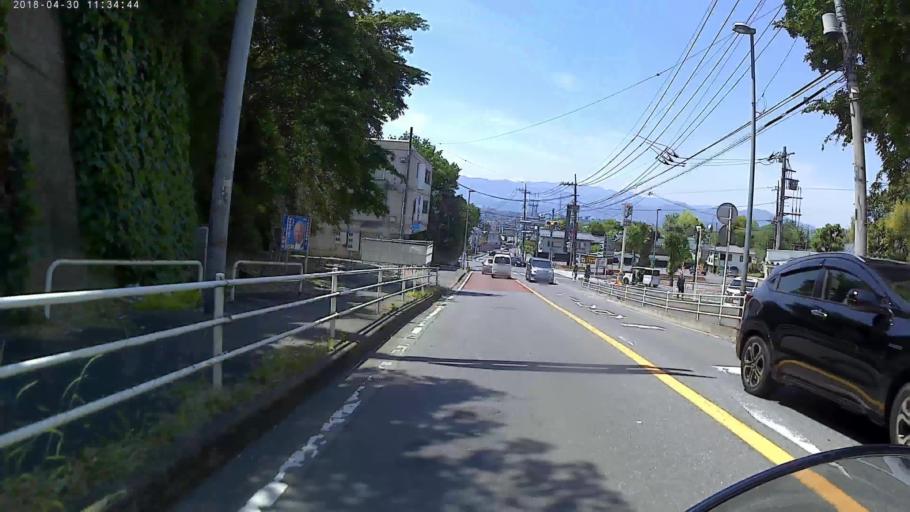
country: JP
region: Kanagawa
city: Zama
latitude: 35.4843
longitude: 139.3973
